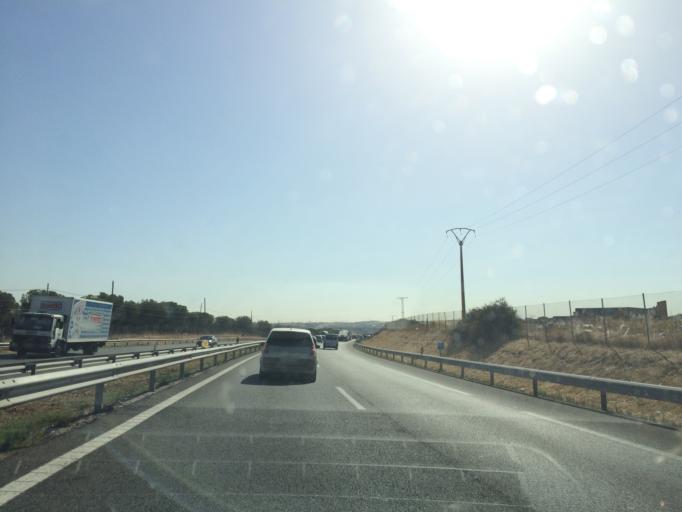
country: ES
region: Madrid
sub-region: Provincia de Madrid
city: Navalcarnero
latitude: 40.2964
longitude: -3.9655
